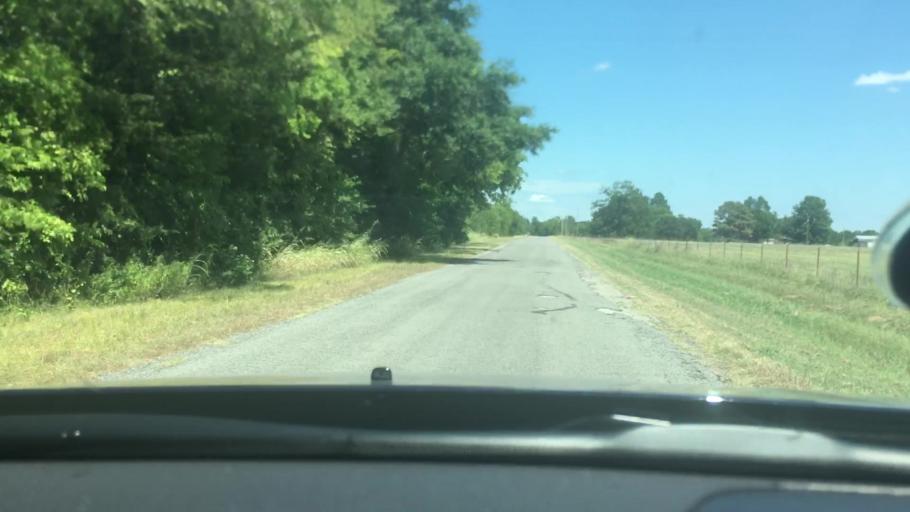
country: US
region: Oklahoma
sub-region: Bryan County
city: Durant
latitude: 33.9896
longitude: -96.2337
